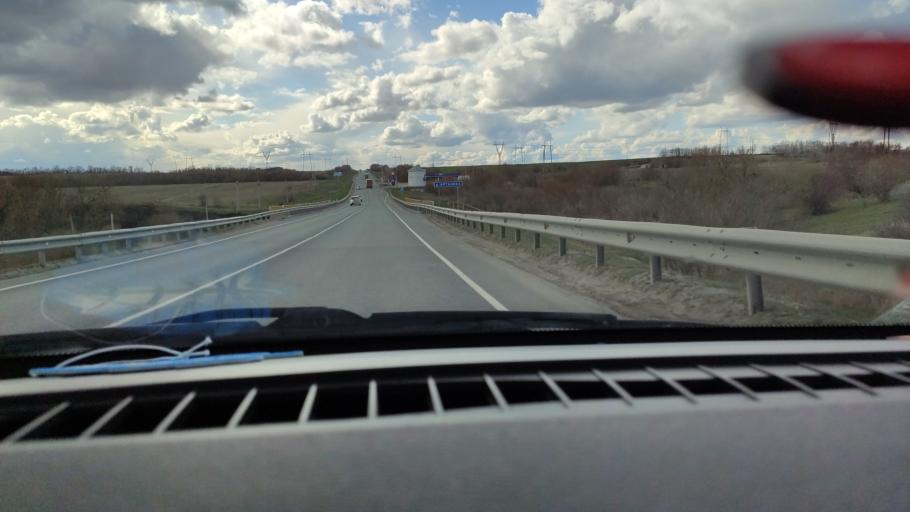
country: RU
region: Saratov
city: Tersa
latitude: 52.0990
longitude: 47.5238
